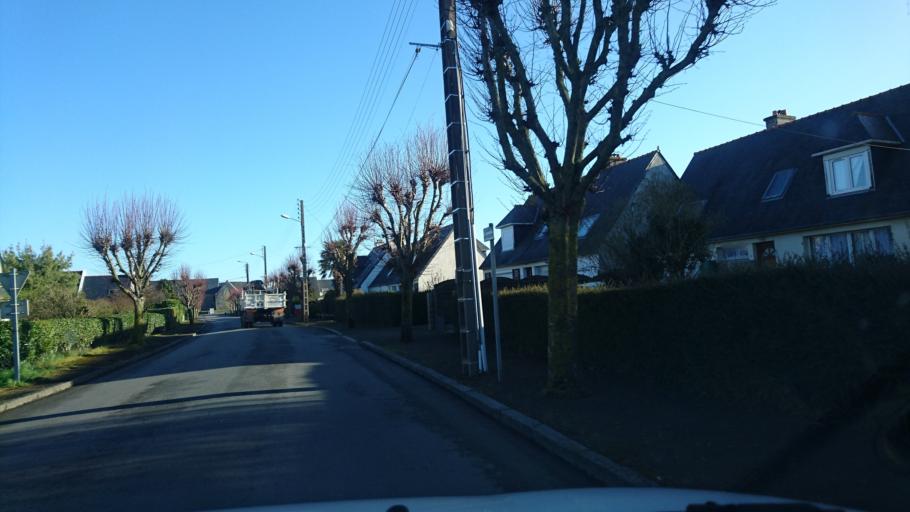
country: FR
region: Brittany
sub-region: Departement d'Ille-et-Vilaine
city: Cherrueix
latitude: 48.6032
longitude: -1.7106
